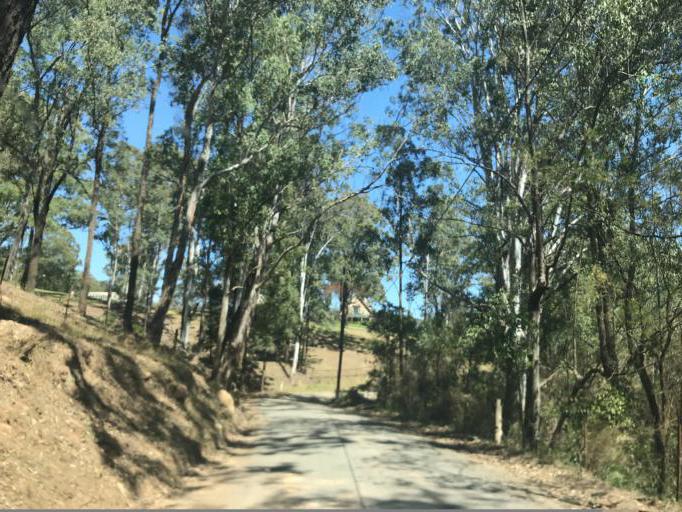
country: AU
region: New South Wales
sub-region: Hornsby Shire
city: Glenorie
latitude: -33.2587
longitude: 150.9739
